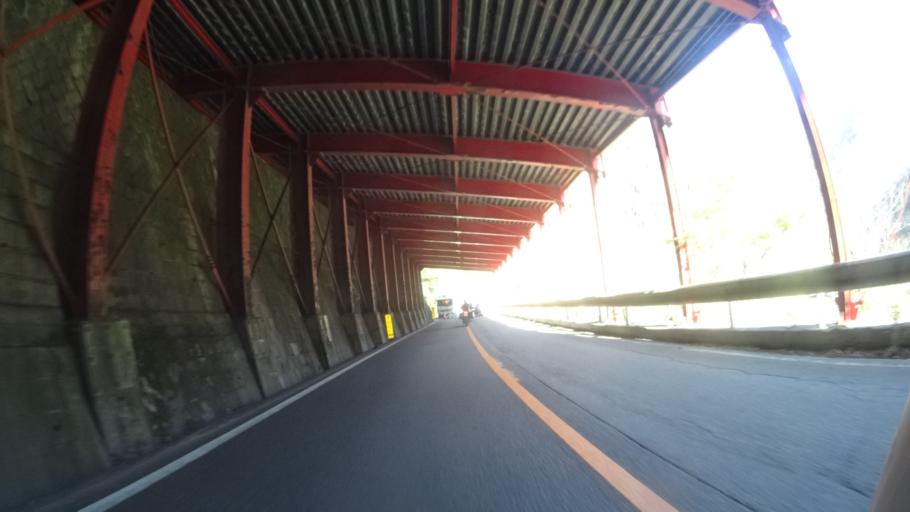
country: JP
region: Fukui
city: Ono
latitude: 35.9496
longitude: 136.6352
